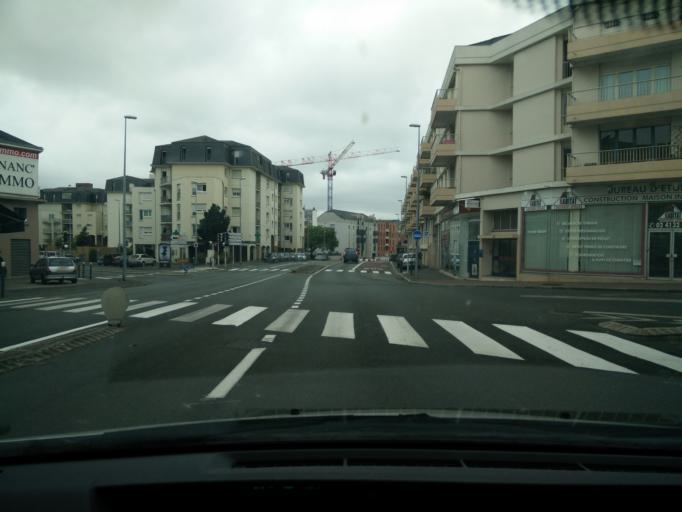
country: FR
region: Pays de la Loire
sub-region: Departement de Maine-et-Loire
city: Angers
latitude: 47.4722
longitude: -0.5407
